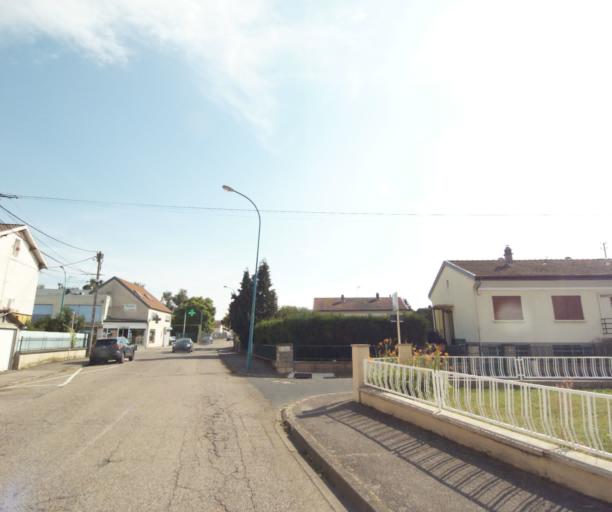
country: FR
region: Lorraine
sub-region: Departement de Meurthe-et-Moselle
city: Luneville
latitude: 48.5853
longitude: 6.5071
